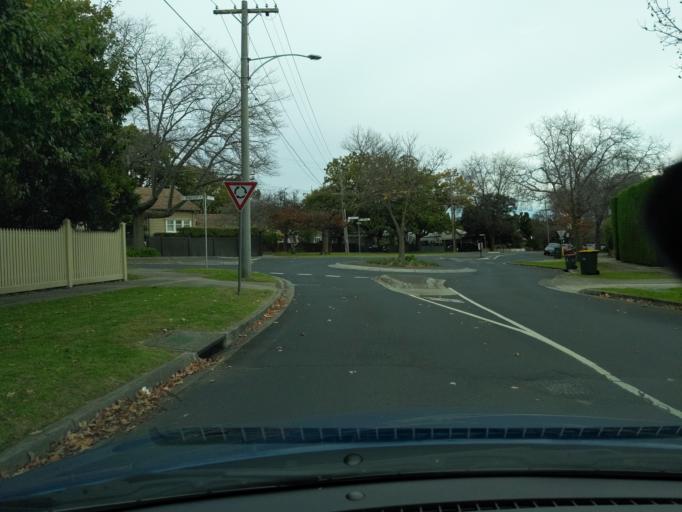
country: AU
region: Victoria
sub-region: Whitehorse
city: Surrey Hills
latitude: -37.8230
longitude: 145.1032
